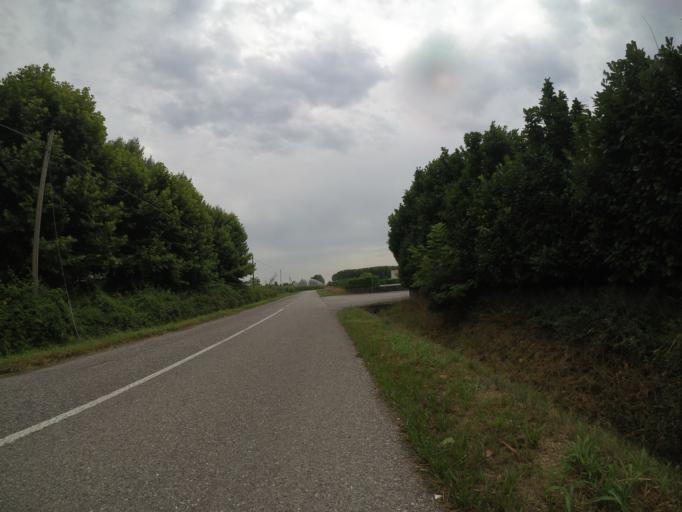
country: IT
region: Friuli Venezia Giulia
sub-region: Provincia di Udine
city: Varmo
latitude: 45.8771
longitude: 12.9940
